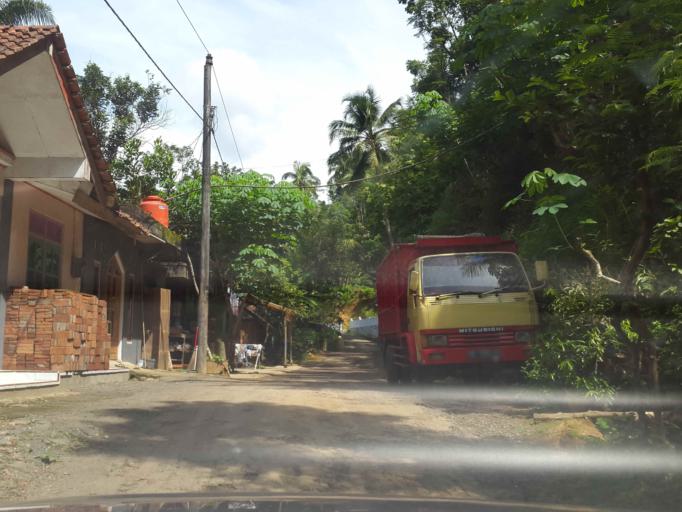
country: ID
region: Central Java
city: Mertoyudan
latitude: -7.6598
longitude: 110.1008
